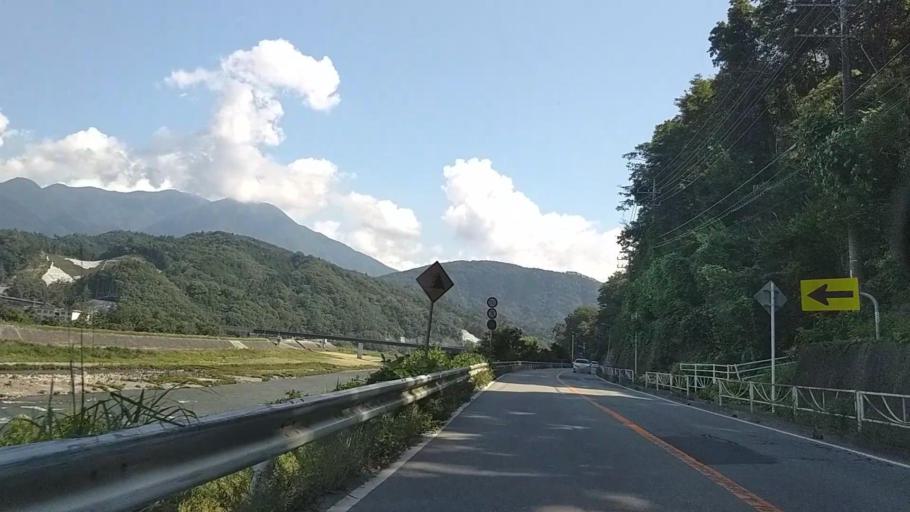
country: JP
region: Yamanashi
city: Ryuo
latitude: 35.4611
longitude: 138.4413
